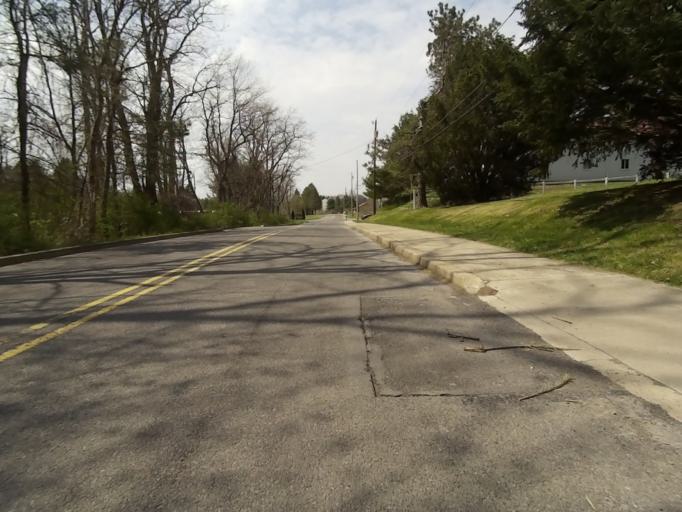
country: US
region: Pennsylvania
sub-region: Centre County
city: State College
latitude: 40.8007
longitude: -77.8831
